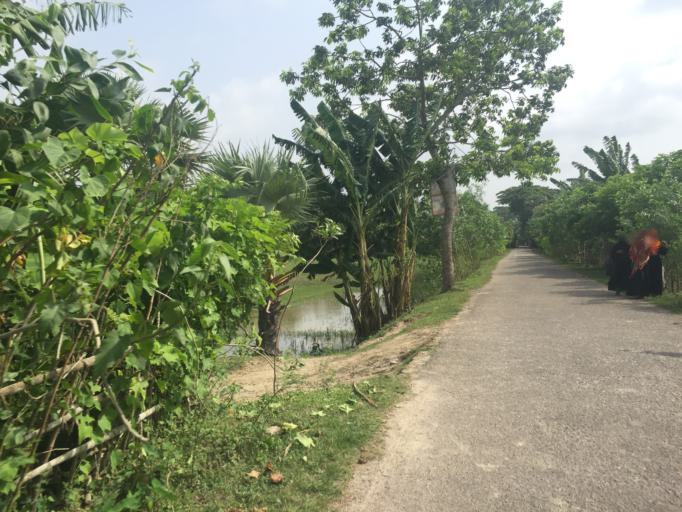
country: BD
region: Barisal
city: Mathba
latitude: 22.2583
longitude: 89.9109
